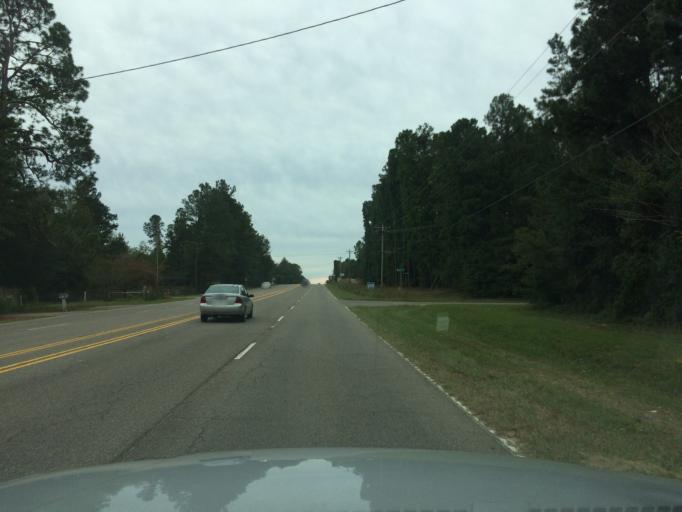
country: US
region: South Carolina
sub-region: Aiken County
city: New Ellenton
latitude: 33.4437
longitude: -81.6866
